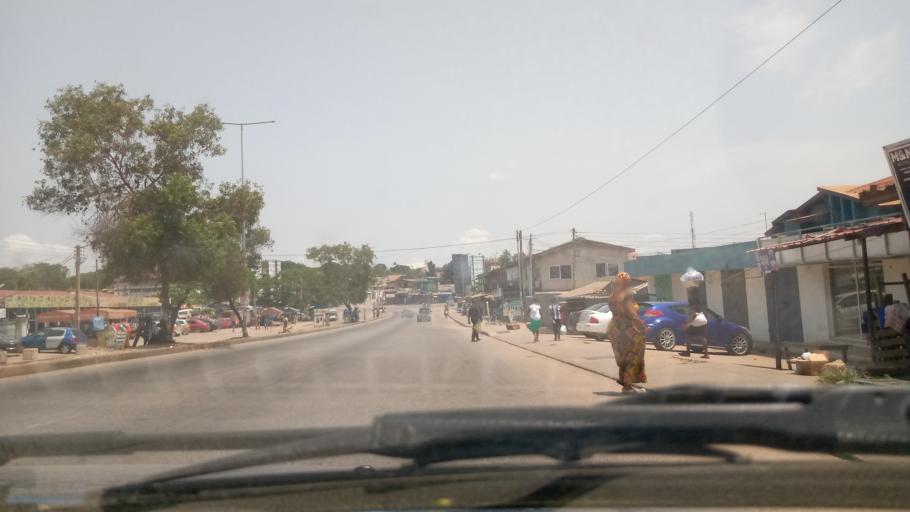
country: GH
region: Greater Accra
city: Accra
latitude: 5.5676
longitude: -0.2428
